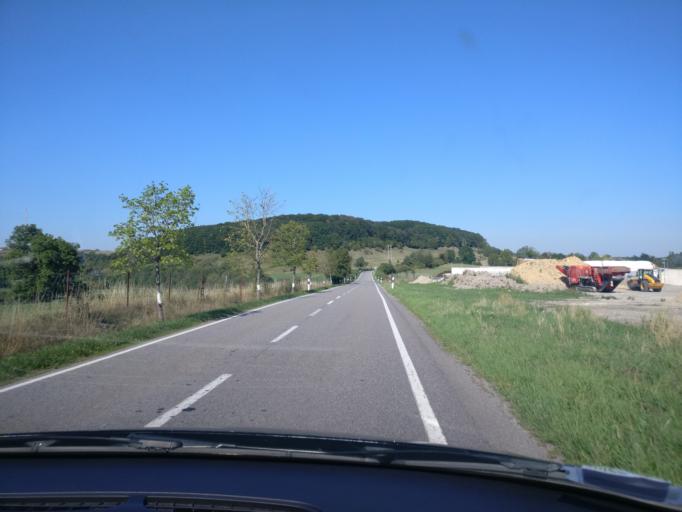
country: LU
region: Grevenmacher
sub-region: Canton de Grevenmacher
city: Junglinster
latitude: 49.6967
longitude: 6.2595
